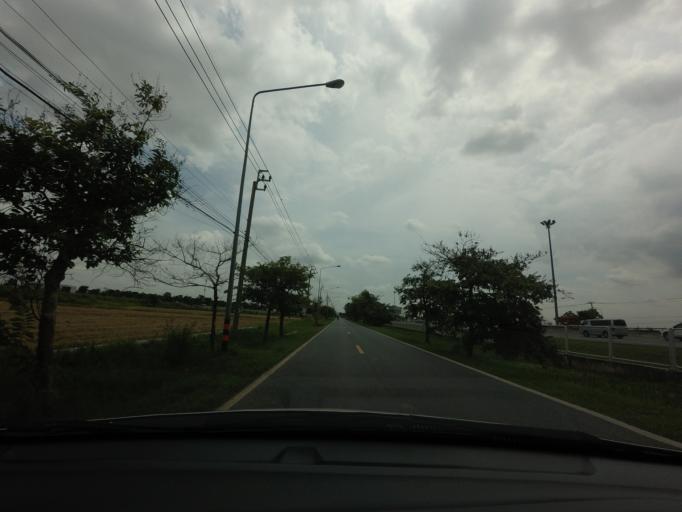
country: TH
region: Bangkok
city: Khan Na Yao
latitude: 13.8739
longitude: 100.6815
